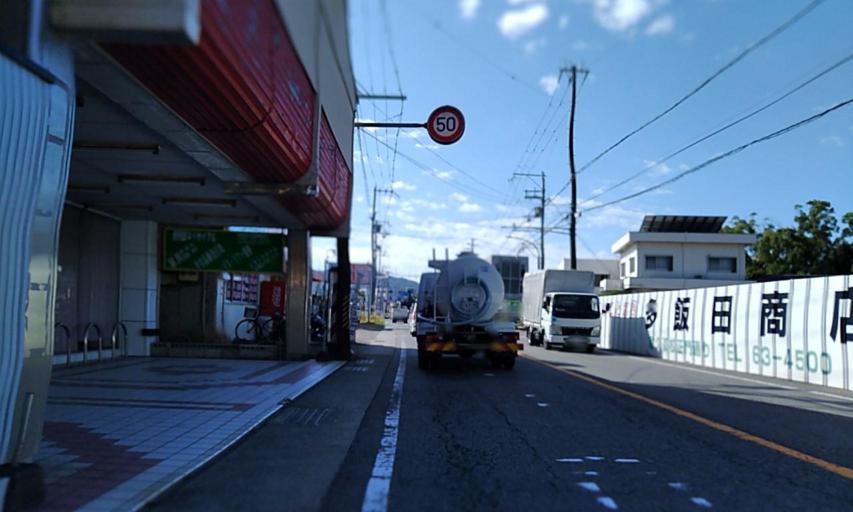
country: JP
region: Wakayama
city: Kainan
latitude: 34.0394
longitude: 135.1864
